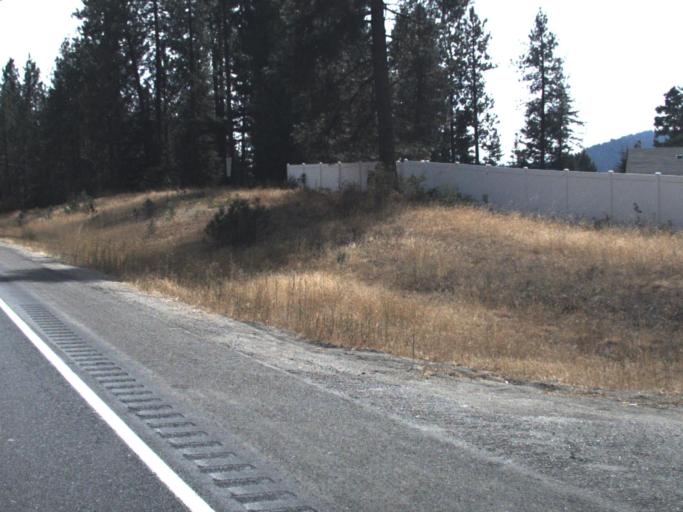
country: US
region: Washington
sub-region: Spokane County
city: Deer Park
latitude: 48.0518
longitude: -117.6137
